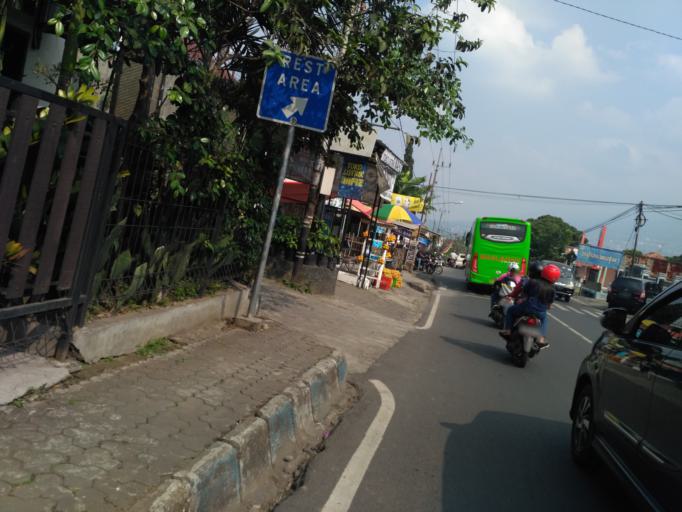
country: ID
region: East Java
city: Batu
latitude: -7.8524
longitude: 112.5275
